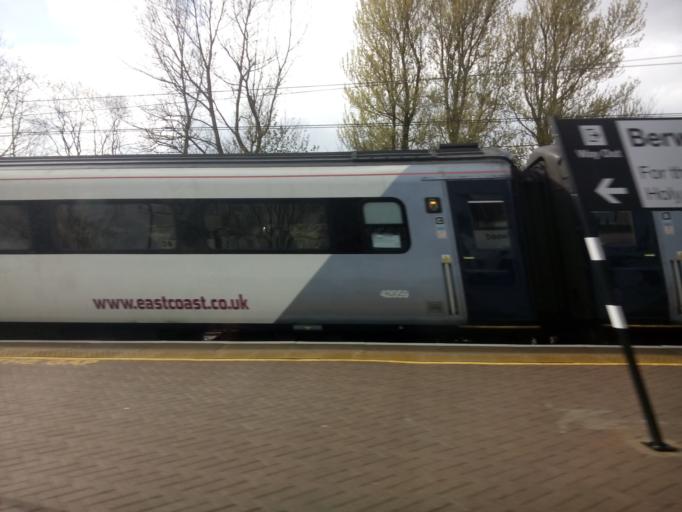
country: GB
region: England
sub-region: Northumberland
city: Berwick-Upon-Tweed
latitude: 55.7755
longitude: -2.0095
